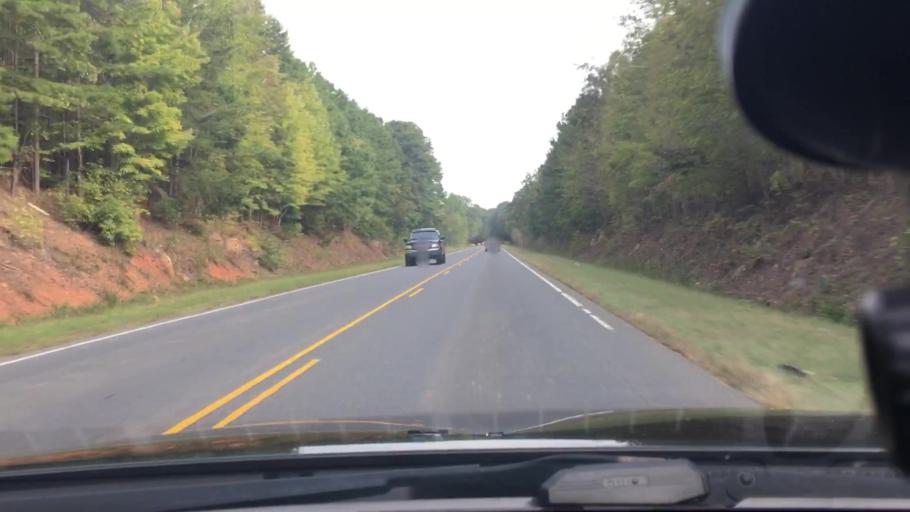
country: US
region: North Carolina
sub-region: Montgomery County
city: Mount Gilead
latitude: 35.3063
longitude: -80.0368
